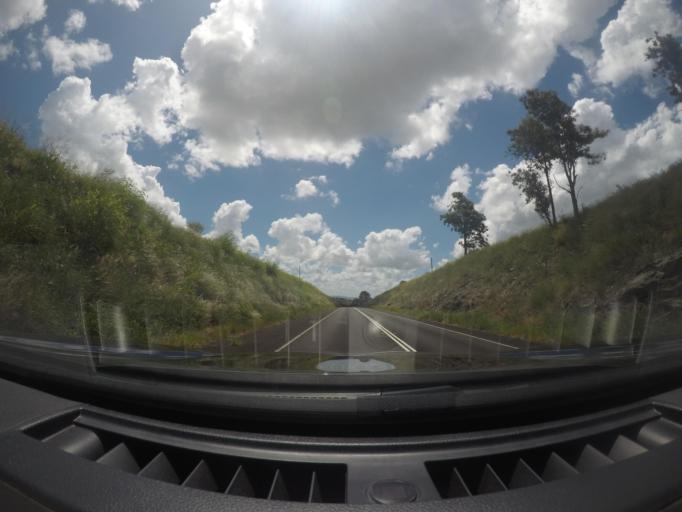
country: AU
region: Queensland
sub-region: Moreton Bay
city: Woodford
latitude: -27.1396
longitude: 152.5174
